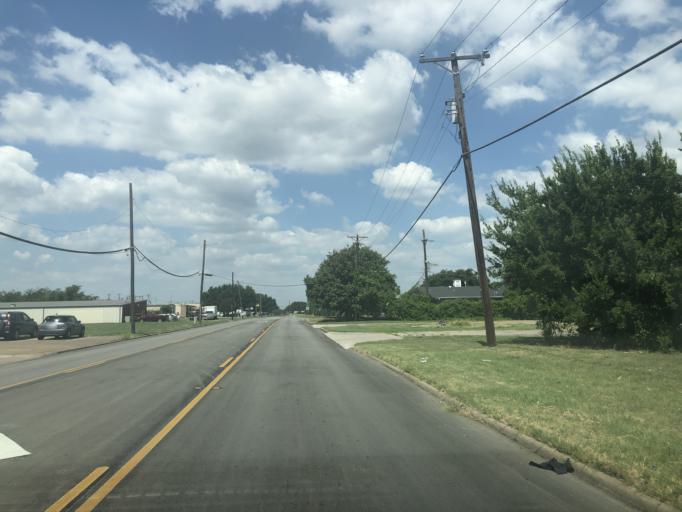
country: US
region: Texas
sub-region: Dallas County
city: Grand Prairie
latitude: 32.7447
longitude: -97.0391
